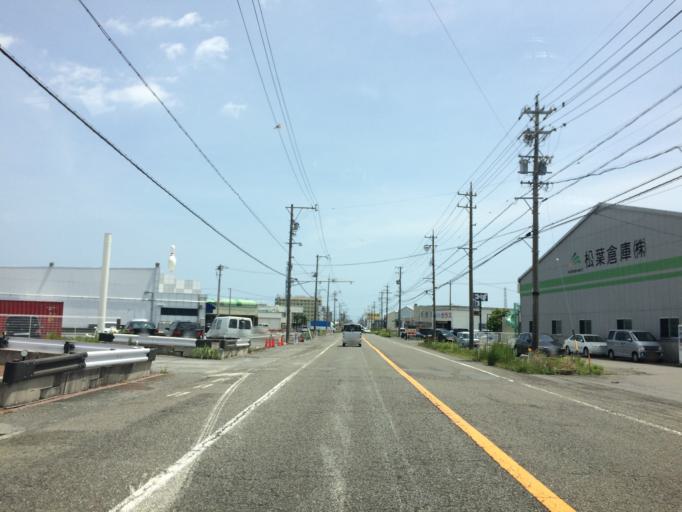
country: JP
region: Shizuoka
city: Fujieda
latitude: 34.8875
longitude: 138.2919
